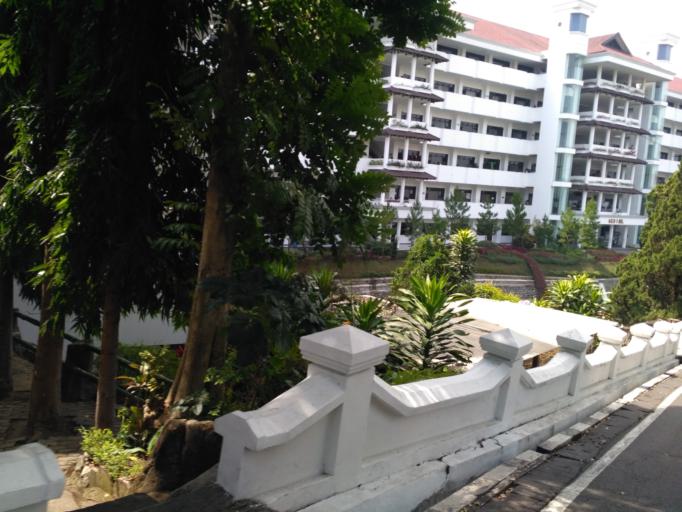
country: ID
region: East Java
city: Malang
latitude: -7.9207
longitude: 112.5974
